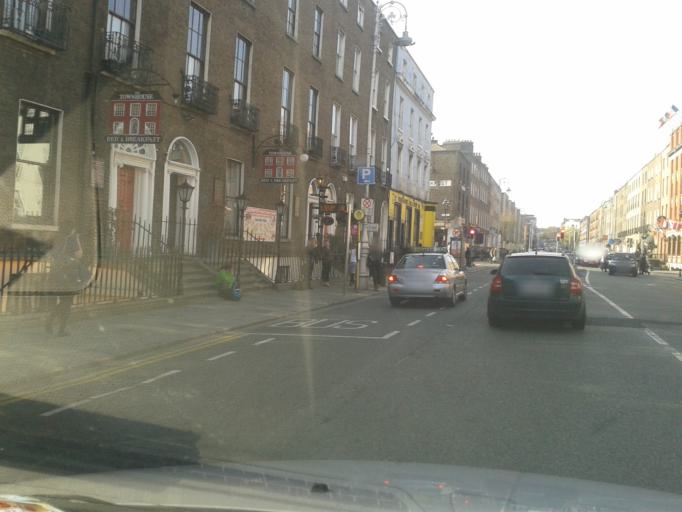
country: IE
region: Leinster
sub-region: Dublin City
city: Dublin
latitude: 53.3502
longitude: -6.2540
